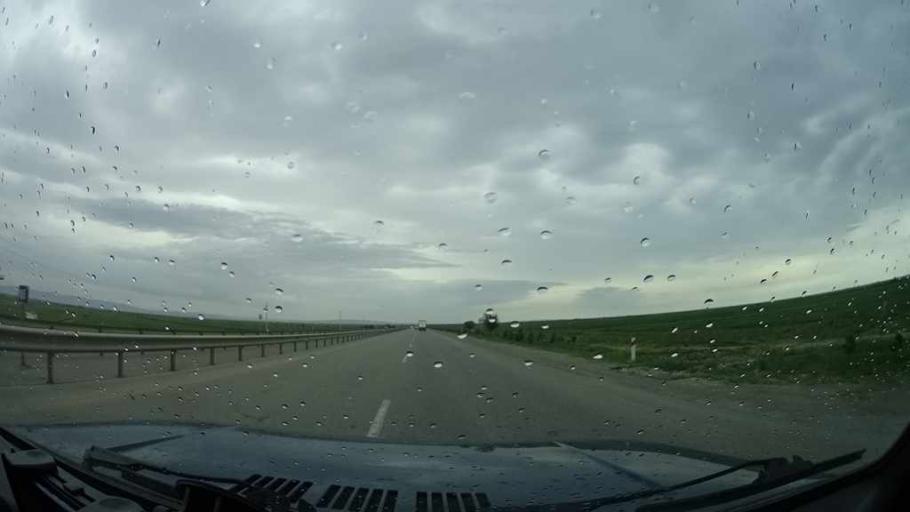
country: AZ
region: Goranboy
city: Goranboy
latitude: 40.6432
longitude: 46.6916
